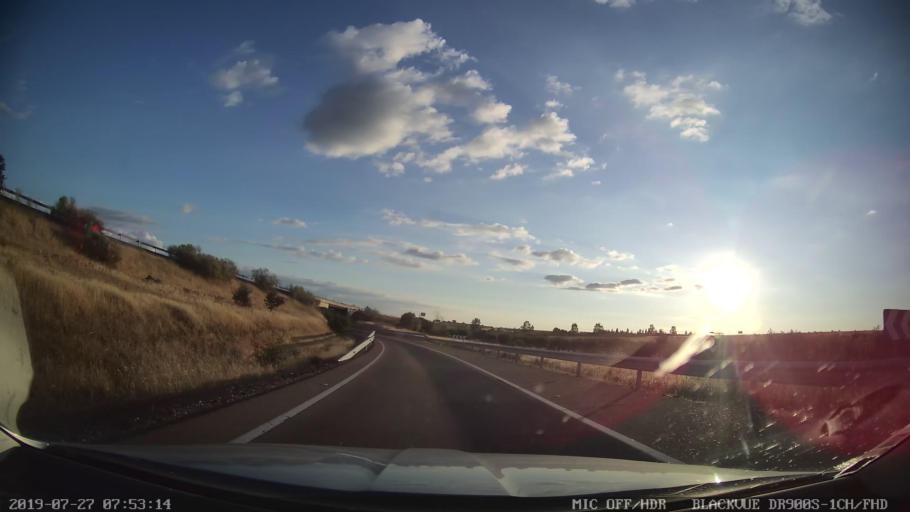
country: ES
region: Extremadura
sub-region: Provincia de Badajoz
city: Trujillanos
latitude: 38.9481
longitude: -6.2837
